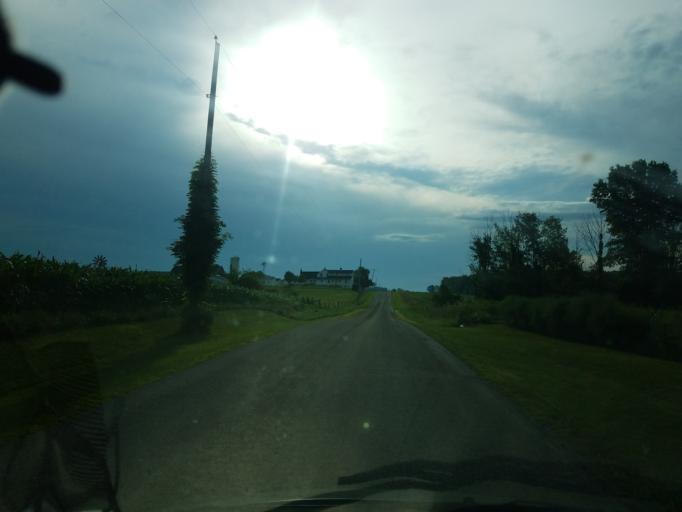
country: US
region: Ohio
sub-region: Huron County
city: Greenwich
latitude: 40.9239
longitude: -82.4853
